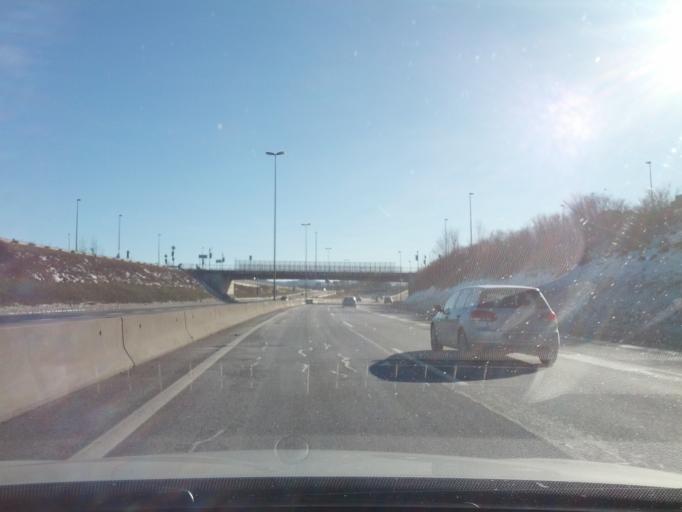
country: SI
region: Ljubljana
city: Ljubljana
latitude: 46.0738
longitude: 14.5468
